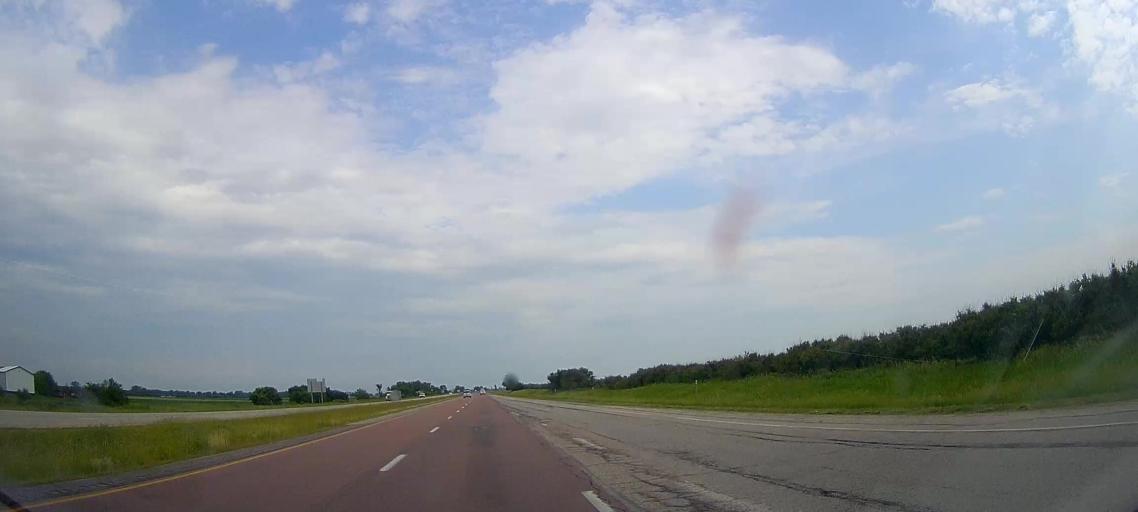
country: US
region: Iowa
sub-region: Monona County
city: Onawa
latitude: 42.0228
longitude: -96.1293
